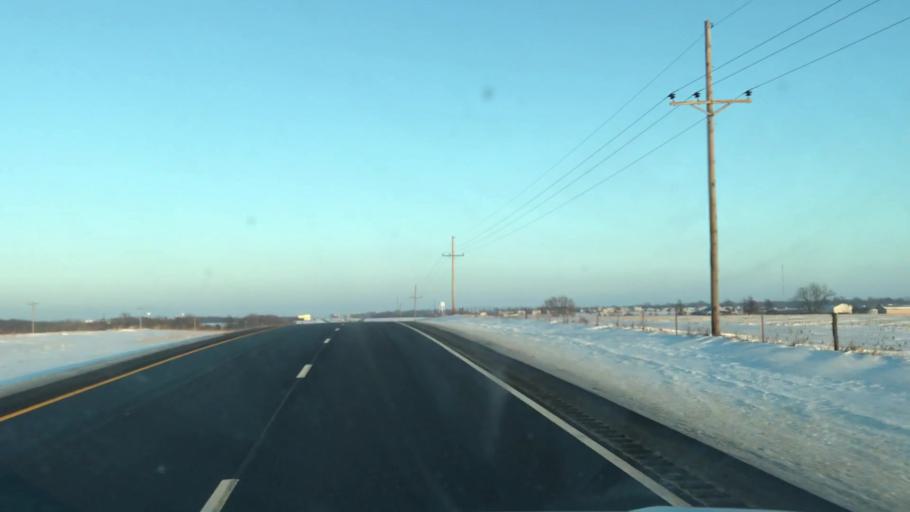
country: US
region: Missouri
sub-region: Clinton County
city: Cameron
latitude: 39.7539
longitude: -94.2753
